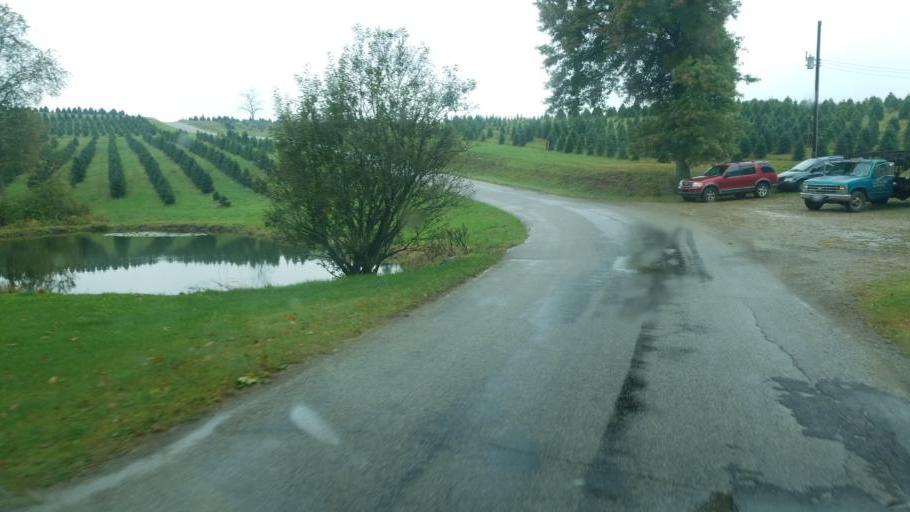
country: US
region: Ohio
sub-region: Sandusky County
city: Bellville
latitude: 40.5747
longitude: -82.4770
